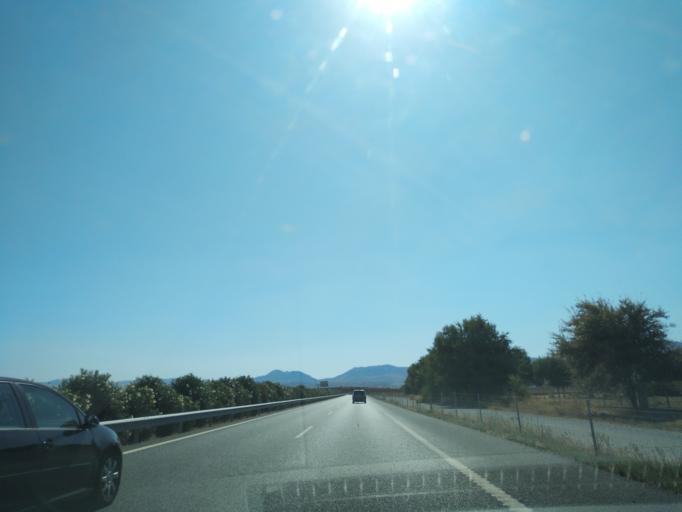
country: ES
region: Andalusia
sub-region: Provincia de Malaga
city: Mollina
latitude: 37.0880
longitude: -4.6239
